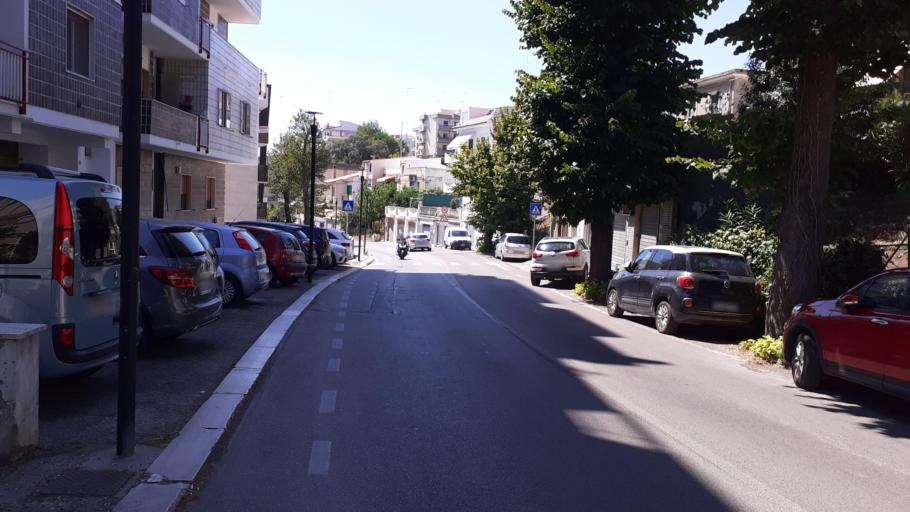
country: IT
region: Molise
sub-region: Provincia di Campobasso
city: Termoli
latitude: 41.9960
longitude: 14.9918
